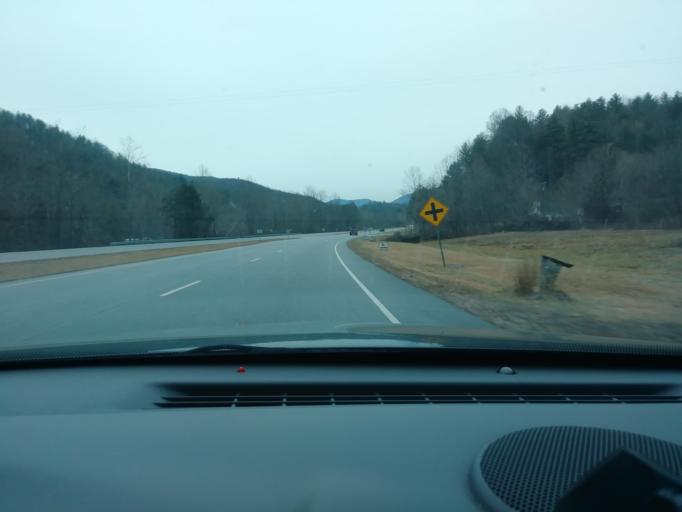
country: US
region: North Carolina
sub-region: Wilkes County
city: Millers Creek
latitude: 36.1814
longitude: -81.3964
